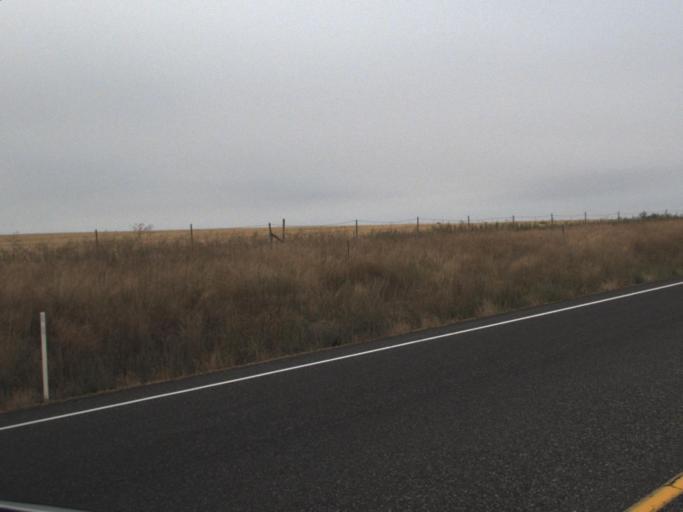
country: US
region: Washington
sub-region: Benton County
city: Prosser
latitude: 46.2022
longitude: -119.7058
